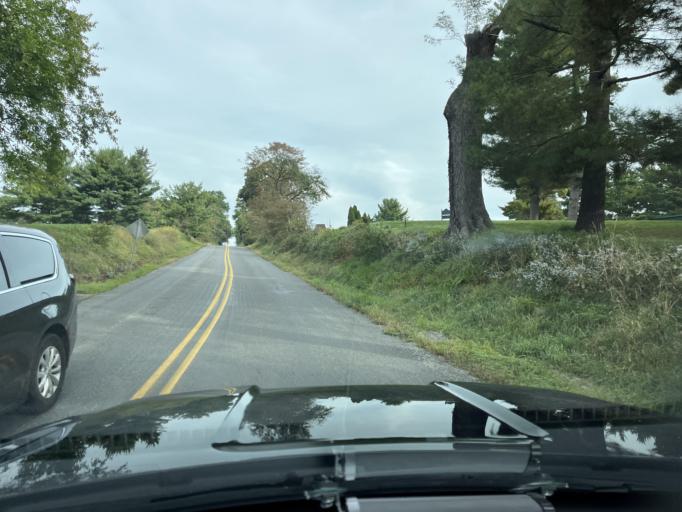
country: US
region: Pennsylvania
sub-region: Fayette County
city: Leith-Hatfield
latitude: 39.8798
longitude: -79.7206
